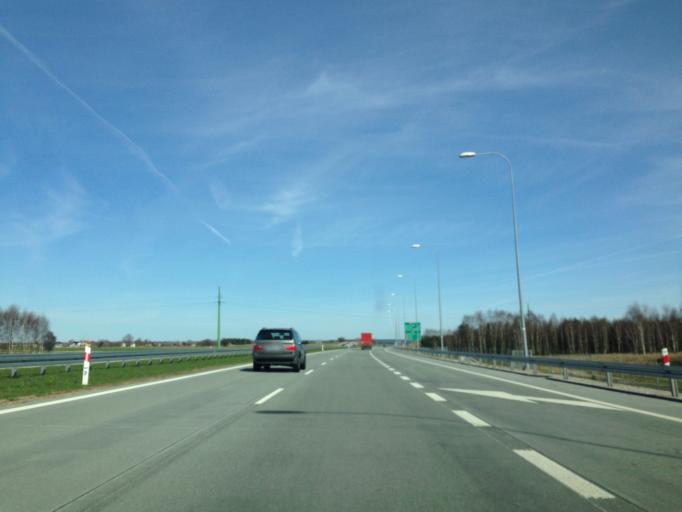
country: PL
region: Lodz Voivodeship
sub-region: Powiat sieradzki
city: Sieradz
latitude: 51.5599
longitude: 18.7316
